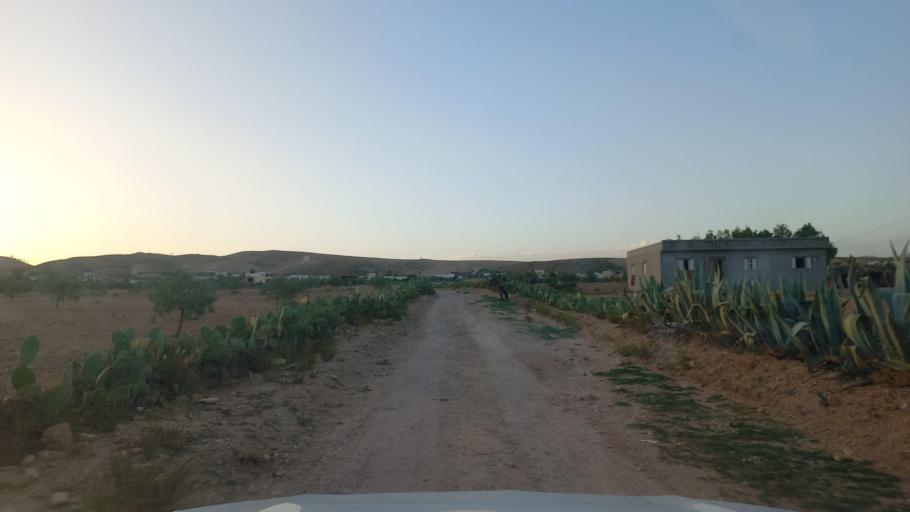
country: TN
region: Al Qasrayn
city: Sbiba
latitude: 35.3738
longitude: 9.0137
